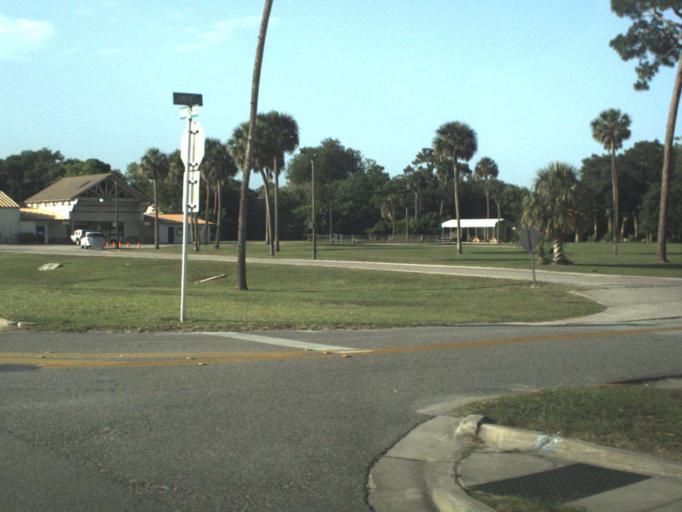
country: US
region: Florida
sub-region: Volusia County
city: Edgewater
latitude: 28.9934
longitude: -80.9086
